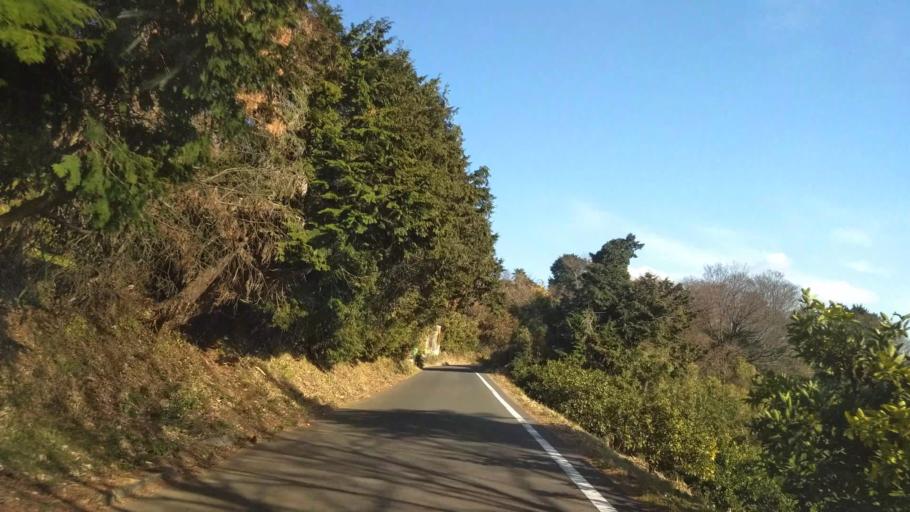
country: JP
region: Kanagawa
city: Hadano
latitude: 35.3700
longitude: 139.2461
